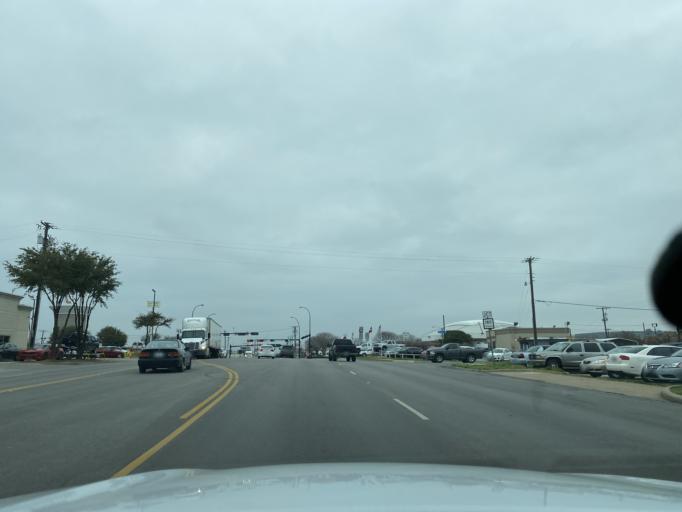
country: US
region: Texas
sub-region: Tarrant County
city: Arlington
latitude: 32.7377
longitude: -97.0973
